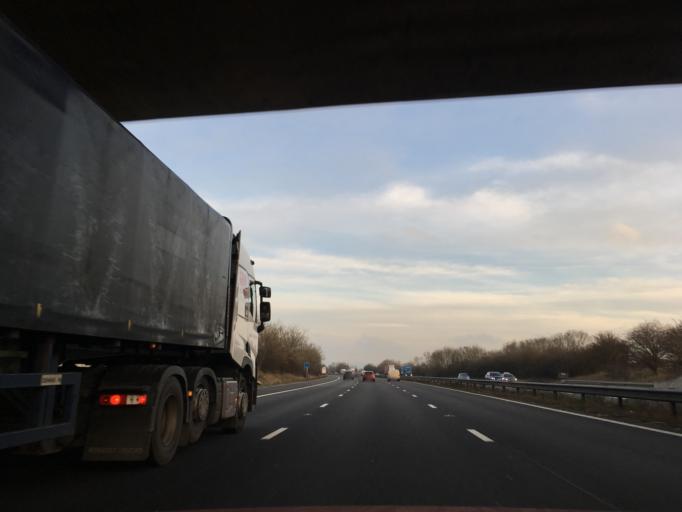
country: GB
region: England
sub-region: Gloucestershire
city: Uckington
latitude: 51.9379
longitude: -2.1299
